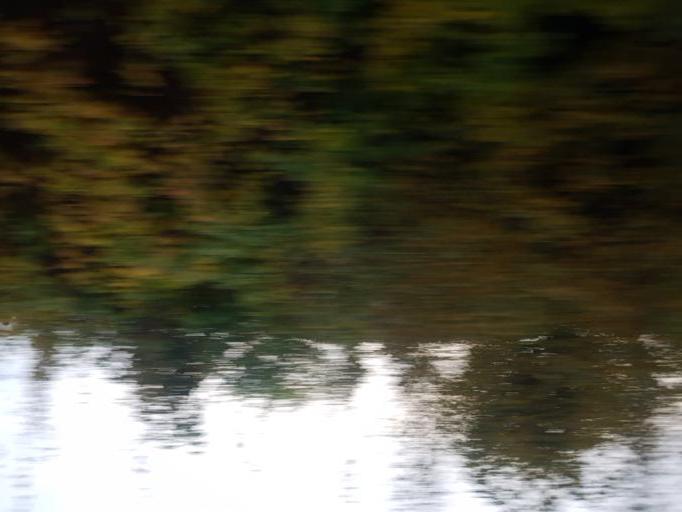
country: NO
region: Sor-Trondelag
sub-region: Melhus
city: Lundamo
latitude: 63.1403
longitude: 10.2669
